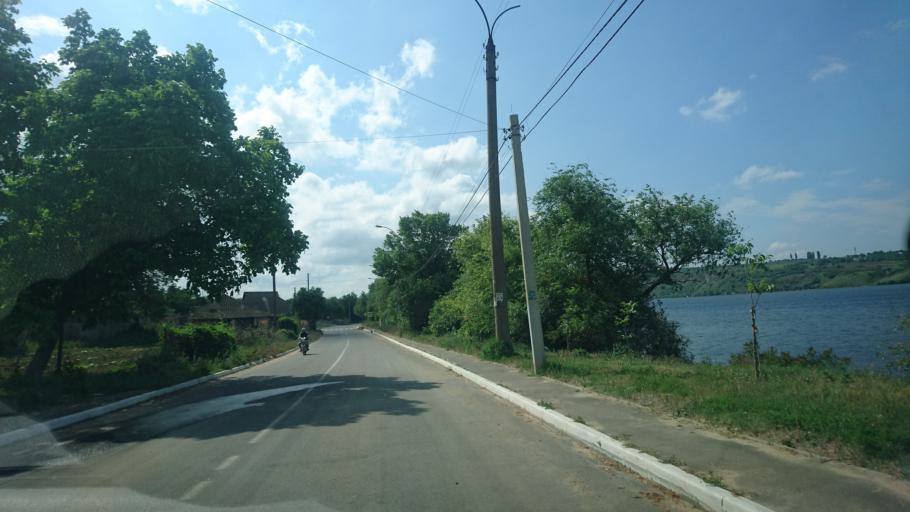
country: MD
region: Telenesti
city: Cocieri
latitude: 47.3534
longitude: 29.1065
